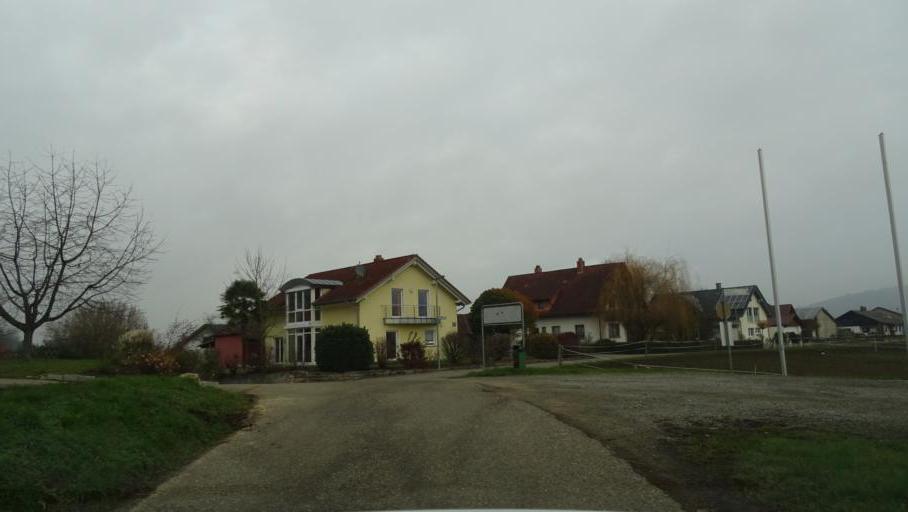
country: DE
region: Baden-Wuerttemberg
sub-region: Karlsruhe Region
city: Neckarzimmern
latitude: 49.3201
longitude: 9.1017
